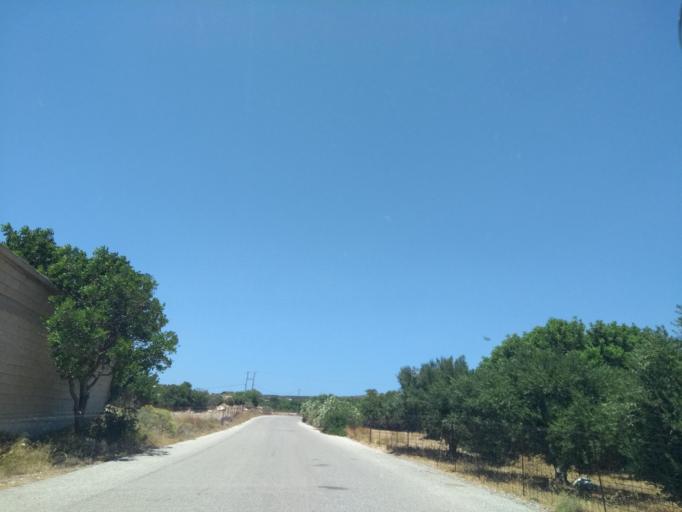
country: GR
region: Crete
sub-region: Nomos Chanias
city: Vryses
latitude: 35.3383
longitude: 23.5450
